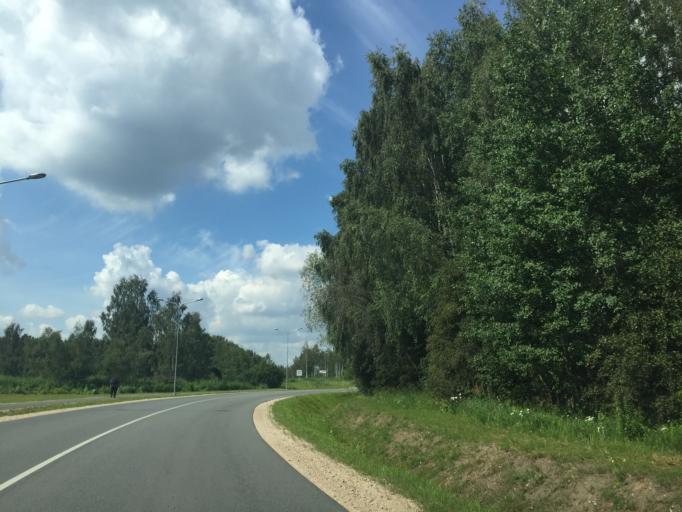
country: LV
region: Kekava
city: Balozi
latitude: 56.8668
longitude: 24.1050
